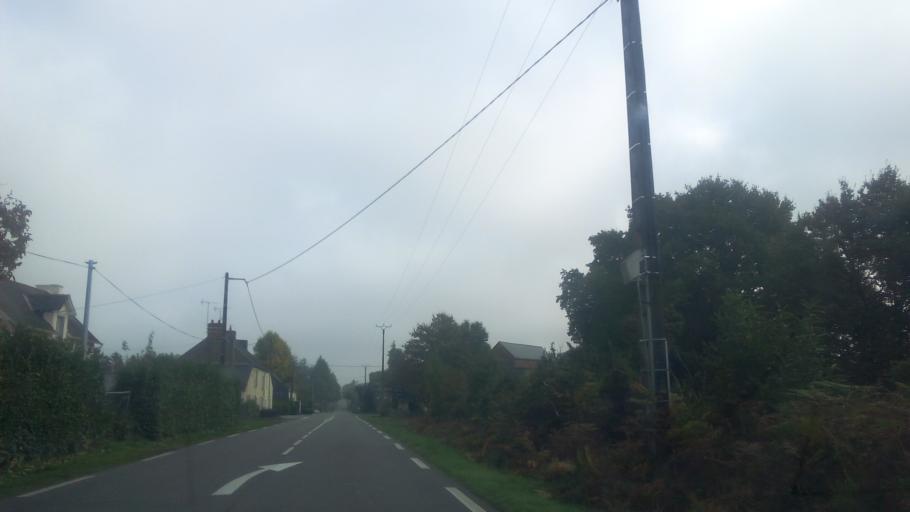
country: FR
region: Pays de la Loire
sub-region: Departement de la Loire-Atlantique
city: Avessac
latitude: 47.6364
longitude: -1.9614
